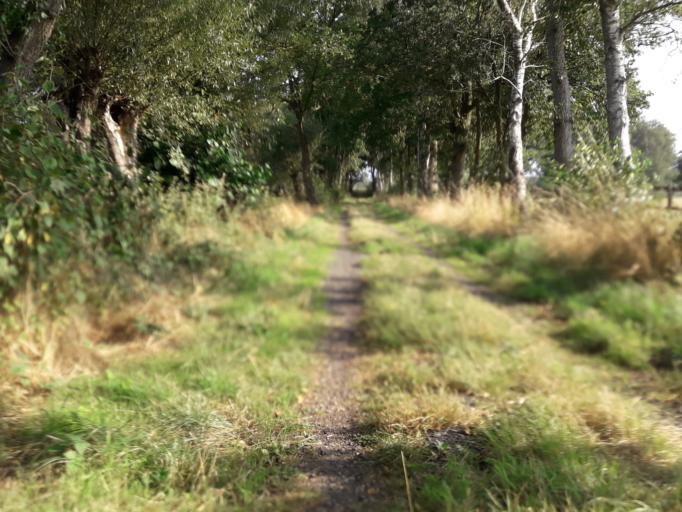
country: DE
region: North Rhine-Westphalia
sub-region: Regierungsbezirk Detmold
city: Hovelhof
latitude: 51.7863
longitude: 8.6774
